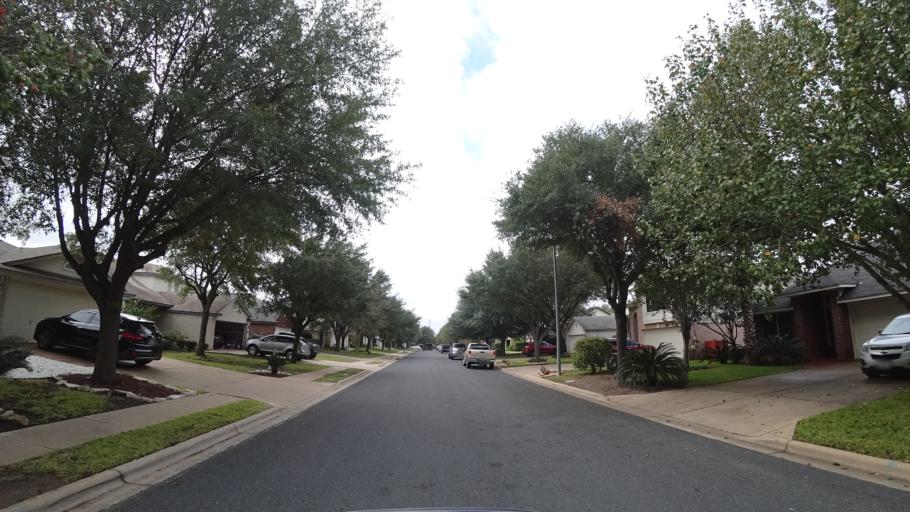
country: US
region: Texas
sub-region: Travis County
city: Shady Hollow
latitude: 30.1861
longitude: -97.8375
